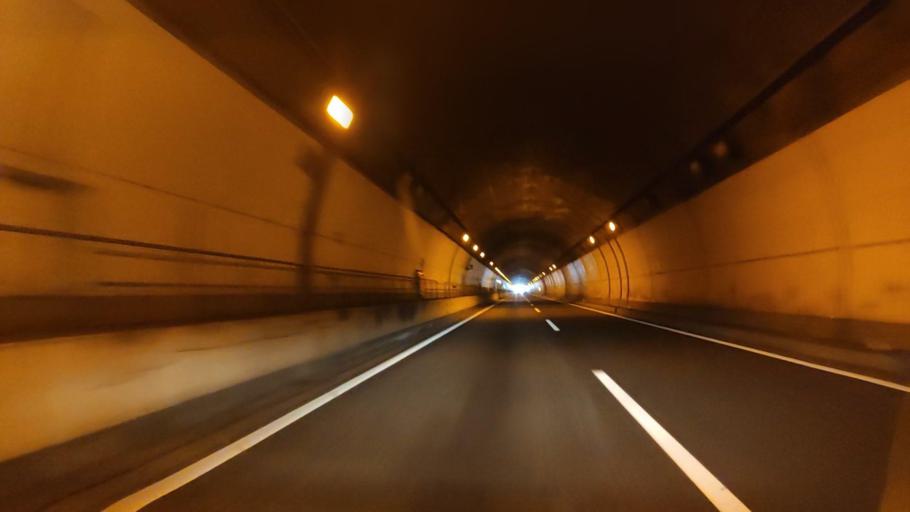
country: JP
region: Akita
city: Hanawa
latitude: 40.0127
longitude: 140.9875
